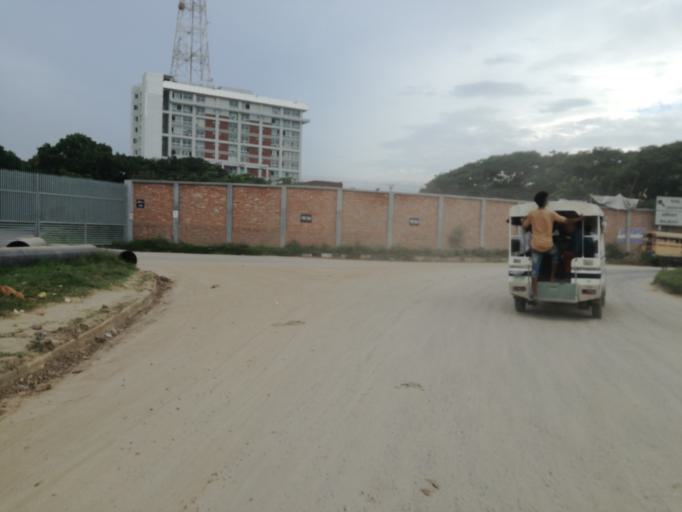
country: BD
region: Dhaka
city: Paltan
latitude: 23.7669
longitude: 90.4246
